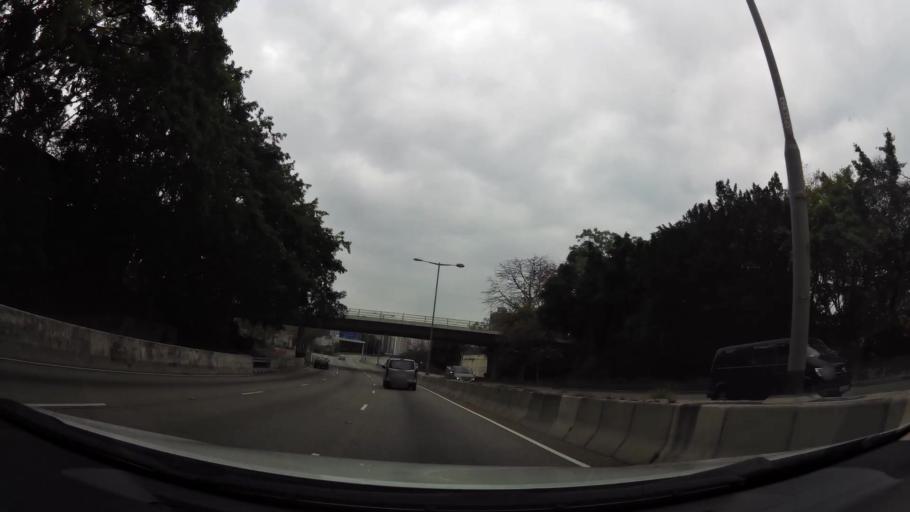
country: HK
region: Yuen Long
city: Yuen Long Kau Hui
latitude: 22.4472
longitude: 114.0133
